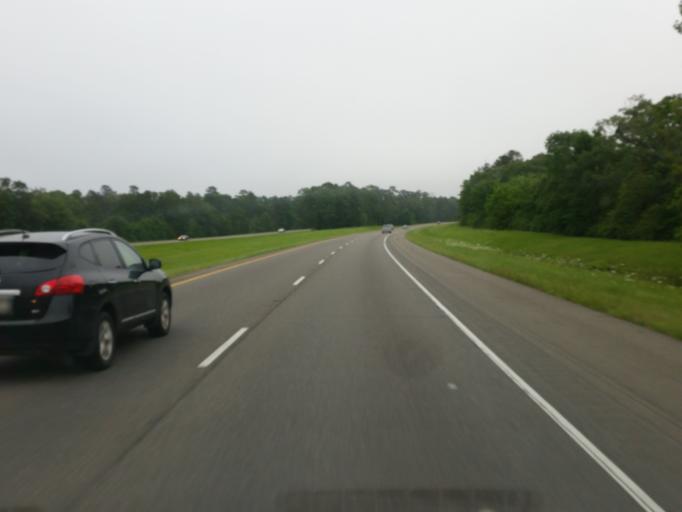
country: US
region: Louisiana
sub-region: Bossier Parish
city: Haughton
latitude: 32.5734
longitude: -93.4826
